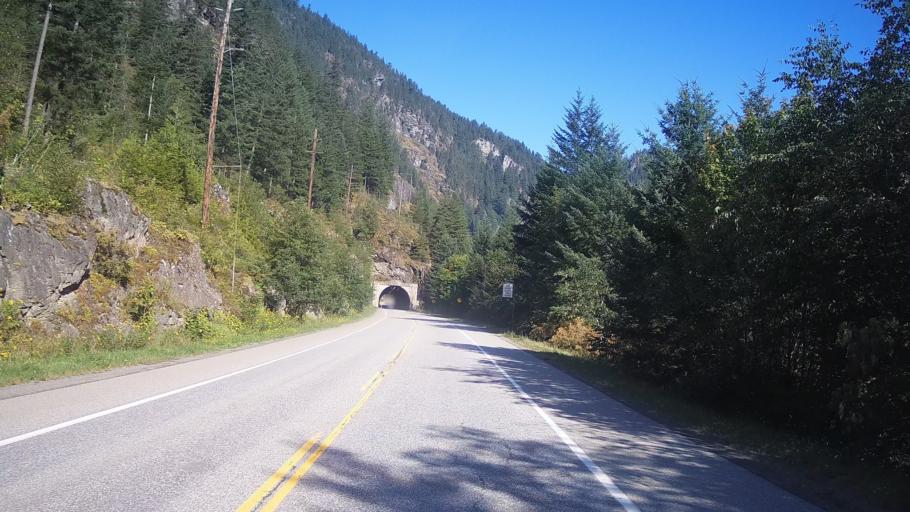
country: CA
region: British Columbia
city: Hope
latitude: 49.6352
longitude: -121.3994
